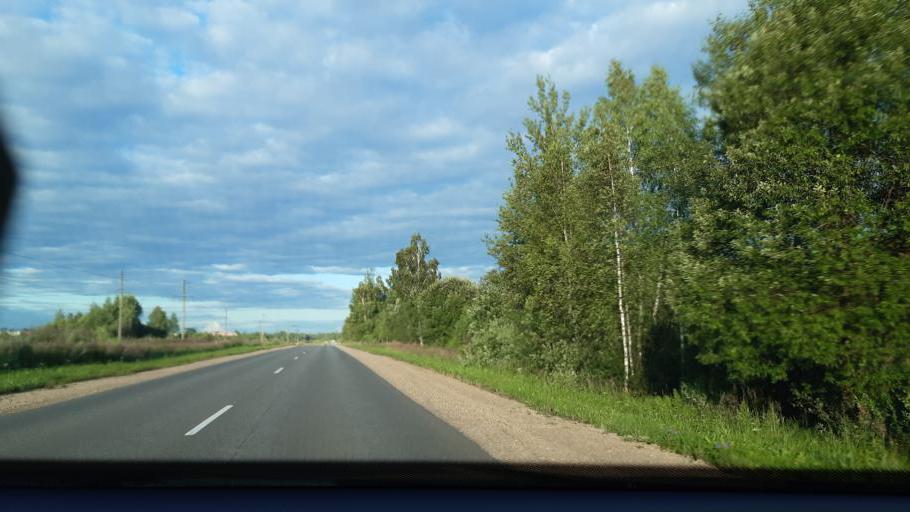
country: RU
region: Smolensk
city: Yel'nya
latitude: 54.5929
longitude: 33.1650
